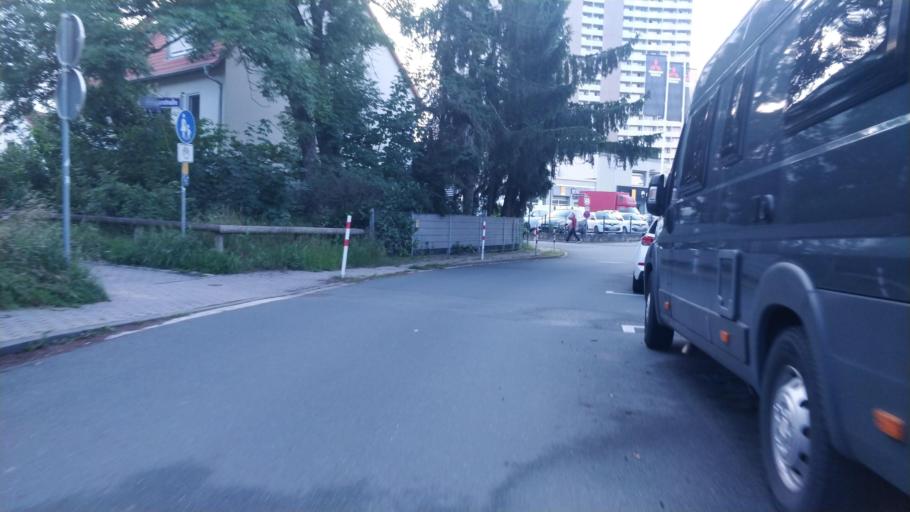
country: DE
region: Bavaria
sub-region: Regierungsbezirk Mittelfranken
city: Erlangen
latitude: 49.6051
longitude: 10.9870
